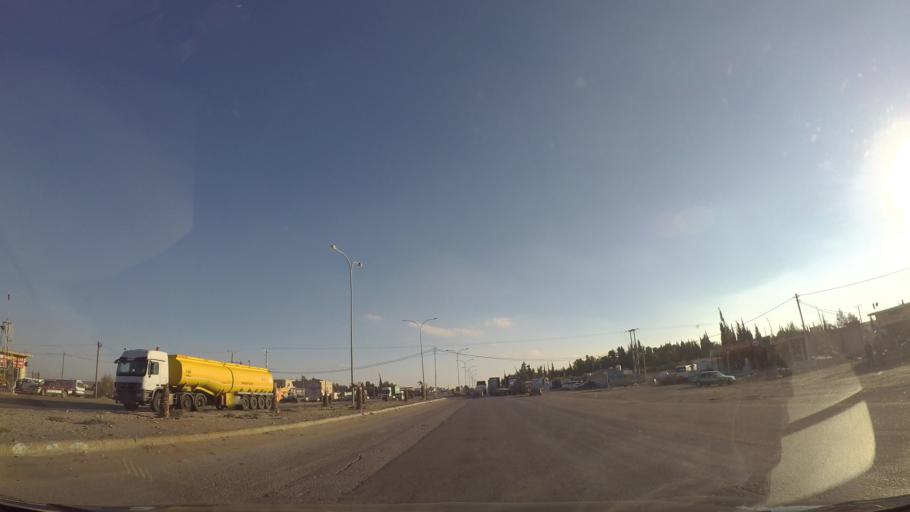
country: JO
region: Tafielah
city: Busayra
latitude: 30.5988
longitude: 35.8045
